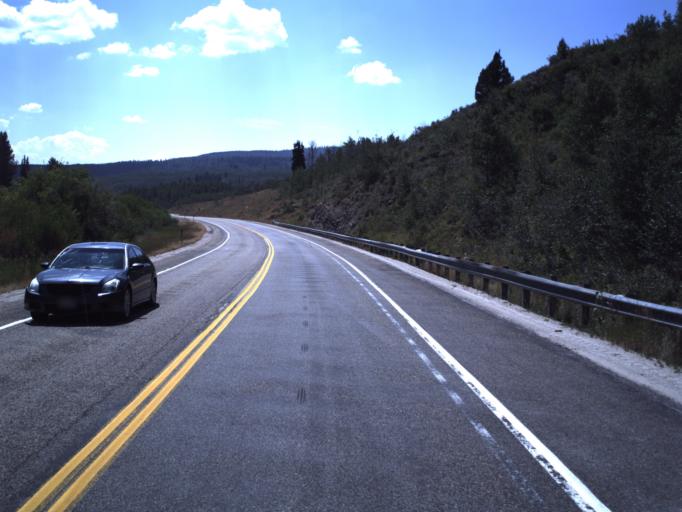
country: US
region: Utah
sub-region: Cache County
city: Richmond
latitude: 41.9358
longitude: -111.5589
